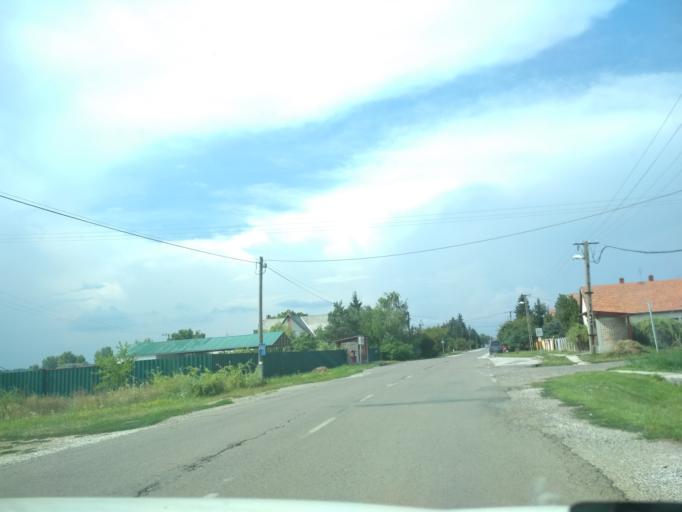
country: HU
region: Jasz-Nagykun-Szolnok
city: Tiszaszolos
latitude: 47.5492
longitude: 20.7211
